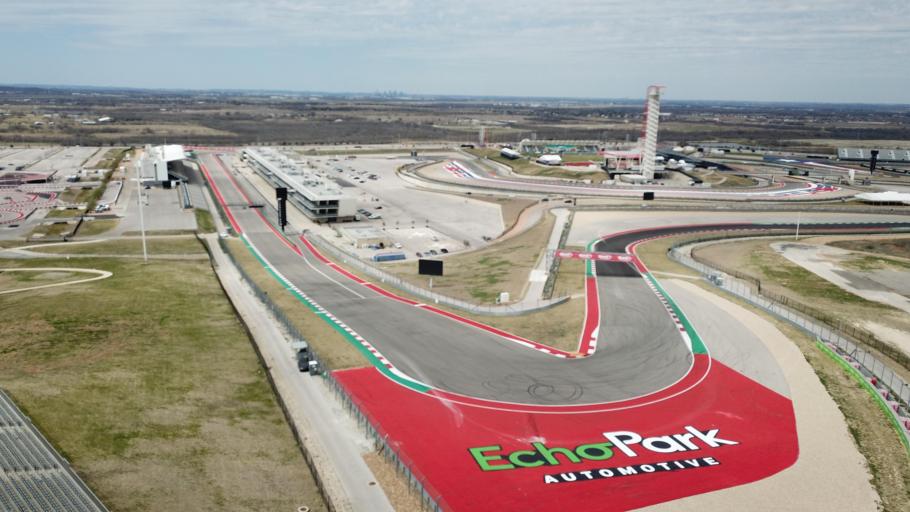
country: US
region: Texas
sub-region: Travis County
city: Garfield
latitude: 30.1291
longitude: -97.6365
